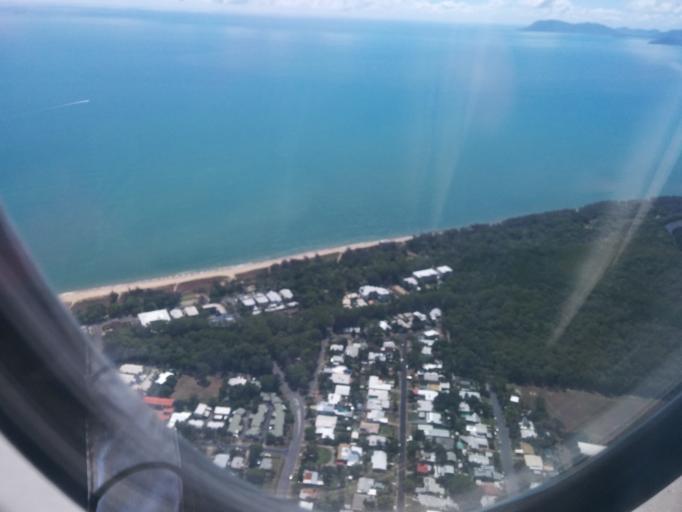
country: AU
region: Queensland
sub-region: Cairns
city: Yorkeys Knob
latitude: -16.8108
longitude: 145.7189
